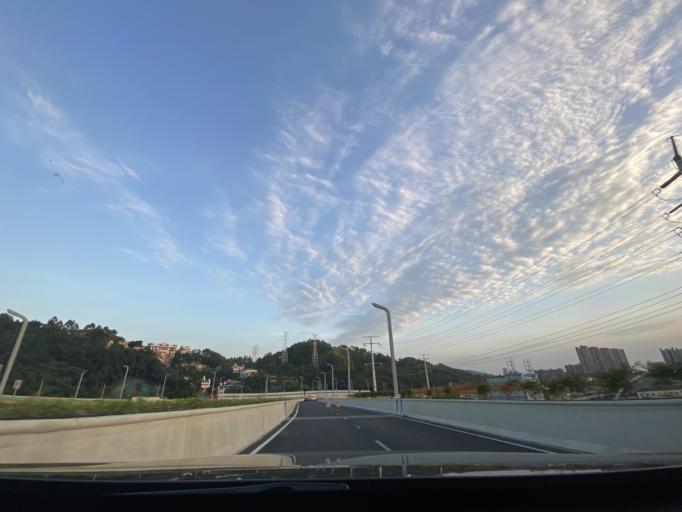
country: CN
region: Sichuan
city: Longquan
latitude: 30.5925
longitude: 104.3028
